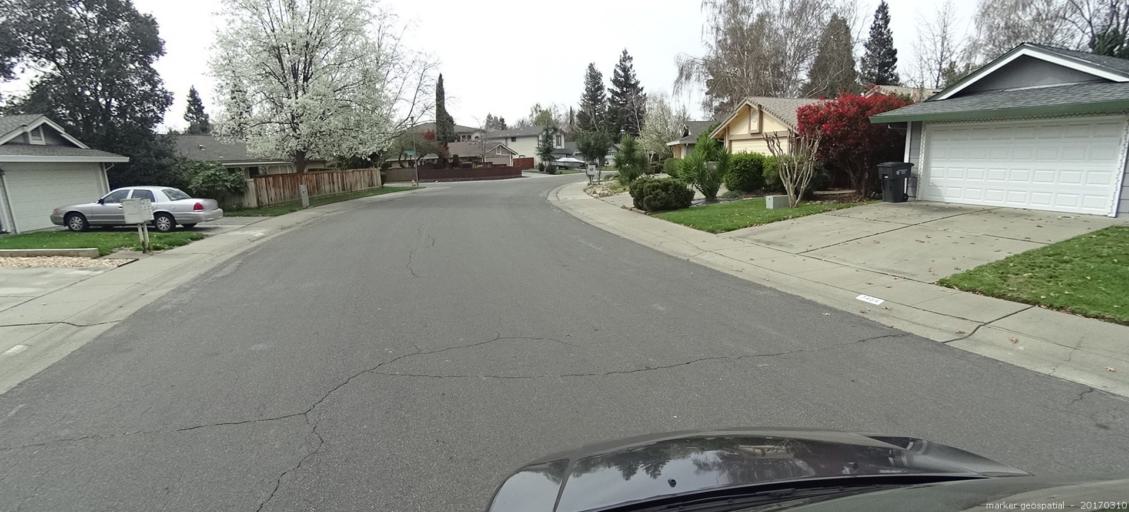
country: US
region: California
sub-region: Sacramento County
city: Parkway
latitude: 38.4865
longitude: -121.5278
